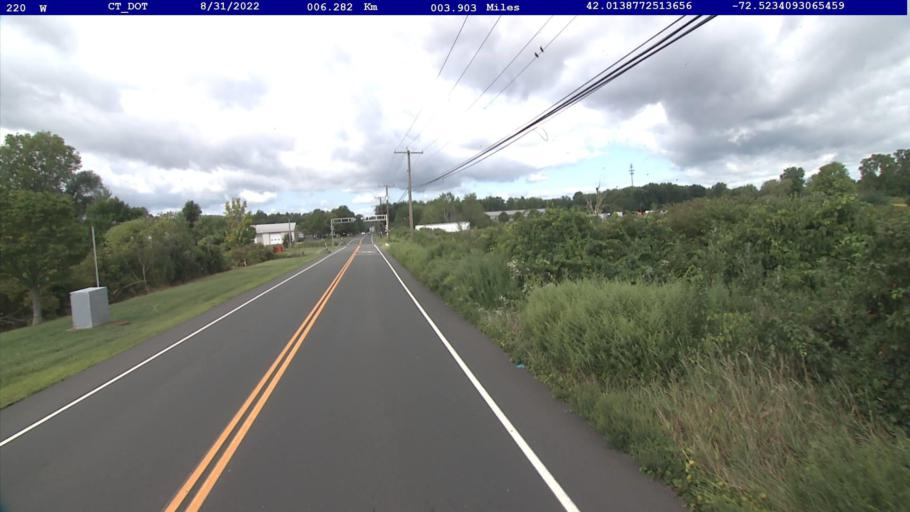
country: US
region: Connecticut
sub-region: Hartford County
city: Hazardville
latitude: 42.0136
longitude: -72.5235
